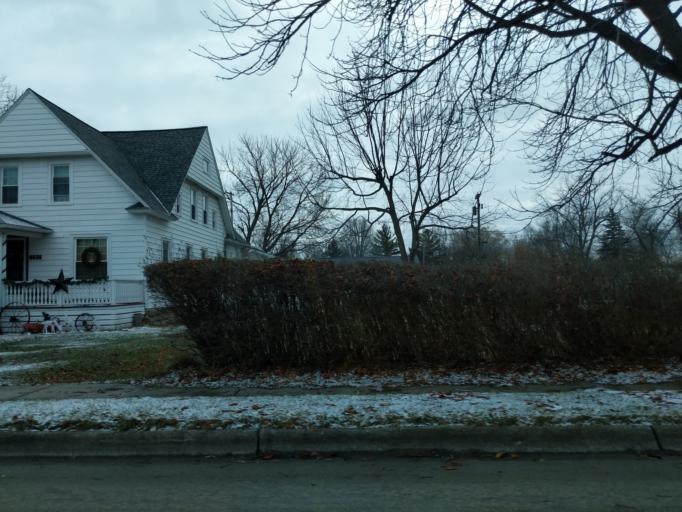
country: US
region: Michigan
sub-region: Sanilac County
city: Marlette
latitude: 43.3277
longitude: -83.0849
